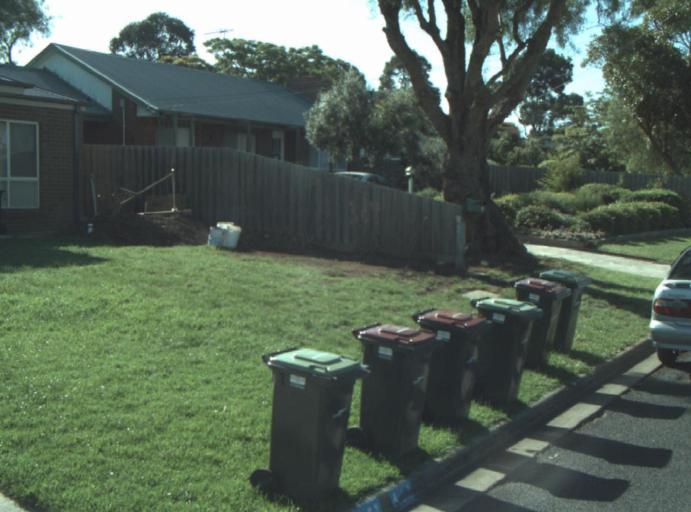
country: AU
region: Victoria
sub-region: Greater Geelong
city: Lara
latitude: -38.0155
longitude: 144.4030
